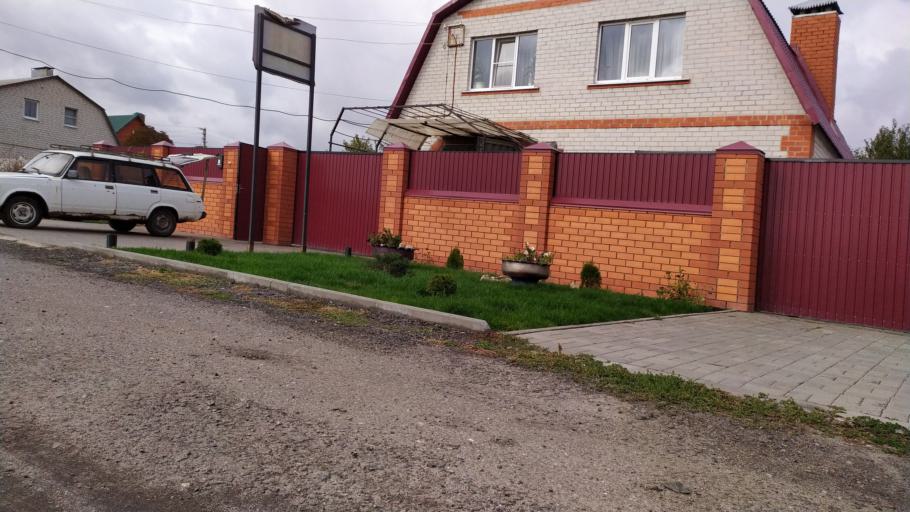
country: RU
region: Kursk
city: Kursk
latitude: 51.6411
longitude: 36.1535
